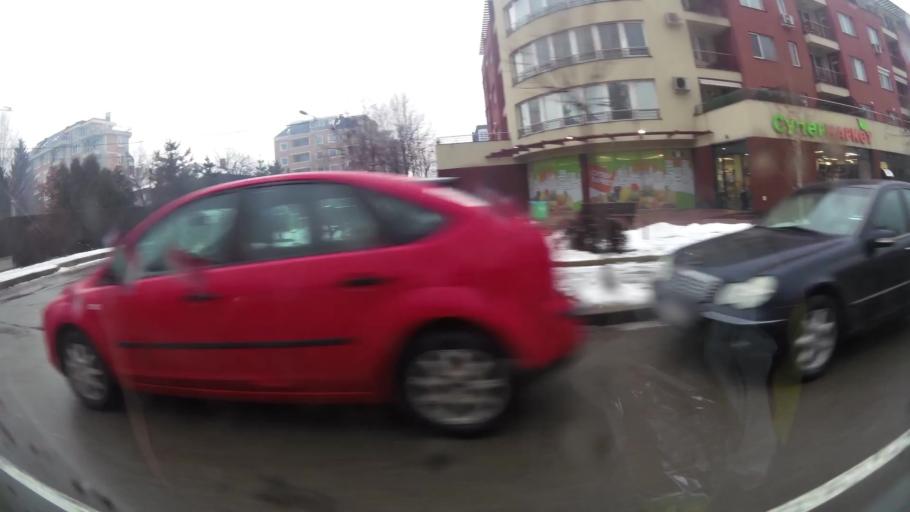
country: BG
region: Sofia-Capital
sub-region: Stolichna Obshtina
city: Sofia
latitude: 42.6744
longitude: 23.2591
